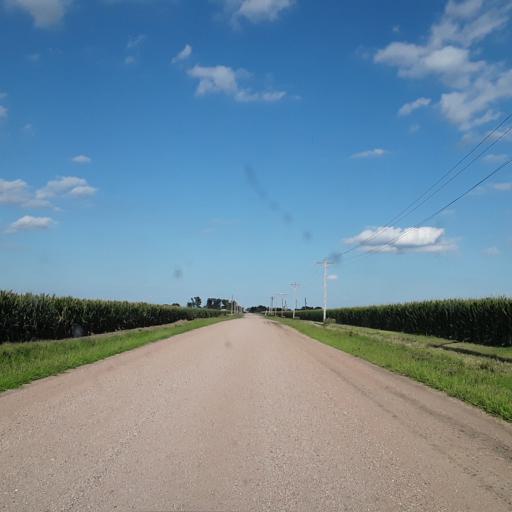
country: US
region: Nebraska
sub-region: Hall County
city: Wood River
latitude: 40.9167
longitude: -98.5743
